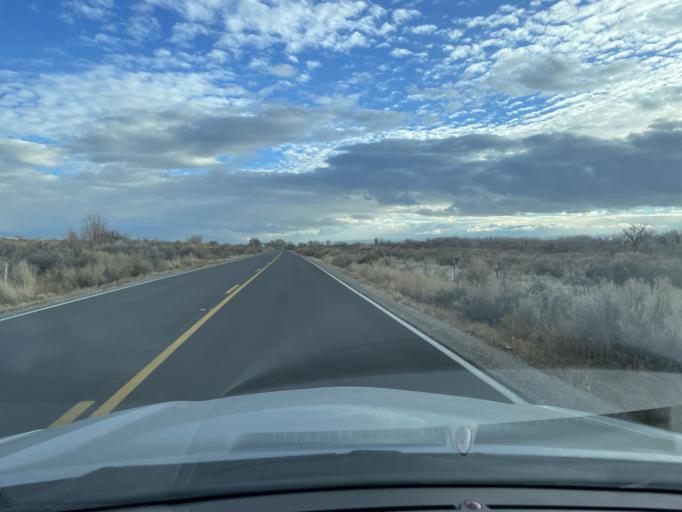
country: US
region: Colorado
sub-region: Montrose County
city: Olathe
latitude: 38.6448
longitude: -107.9941
